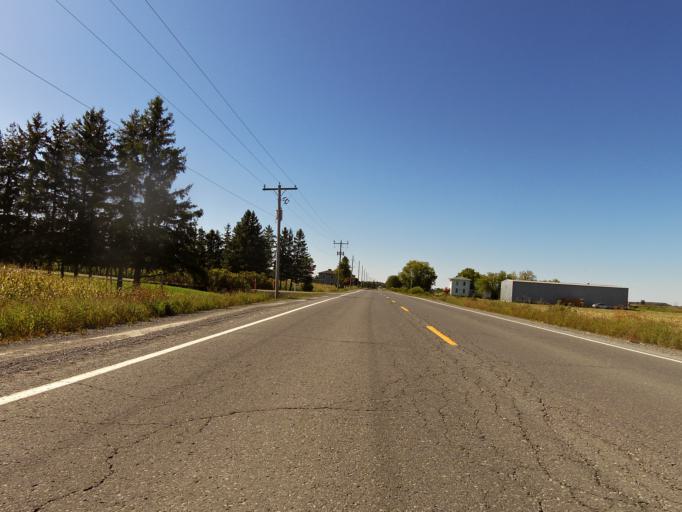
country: CA
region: Ontario
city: Casselman
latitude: 45.2477
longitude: -75.1461
